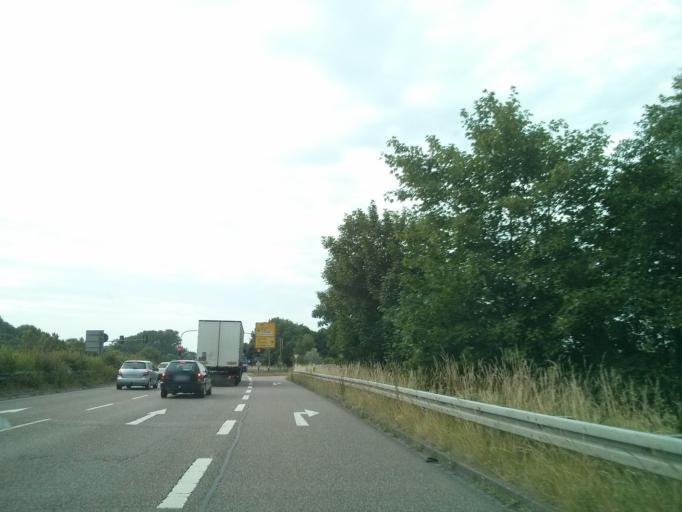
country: DE
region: Baden-Wuerttemberg
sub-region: Karlsruhe Region
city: Bischweier
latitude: 48.8199
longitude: 8.2932
